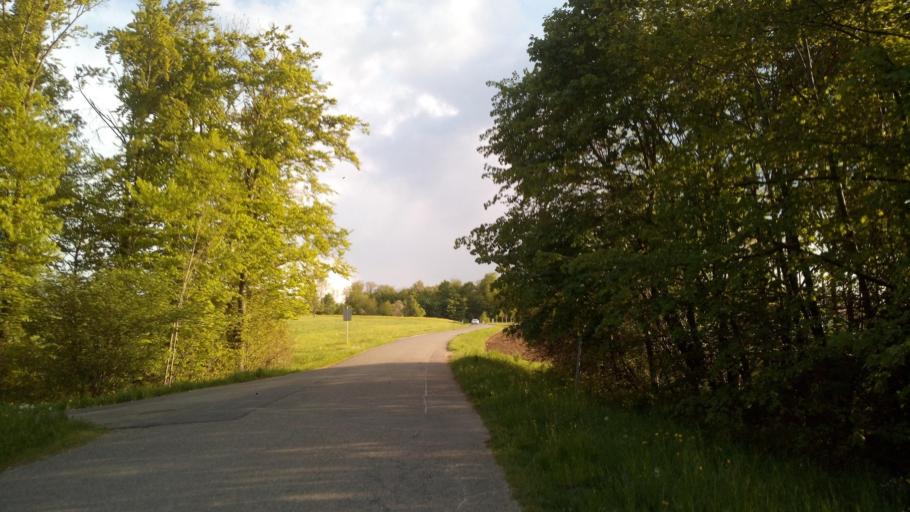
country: DE
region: Baden-Wuerttemberg
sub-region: Regierungsbezirk Stuttgart
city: Salach
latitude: 48.7033
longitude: 9.7519
